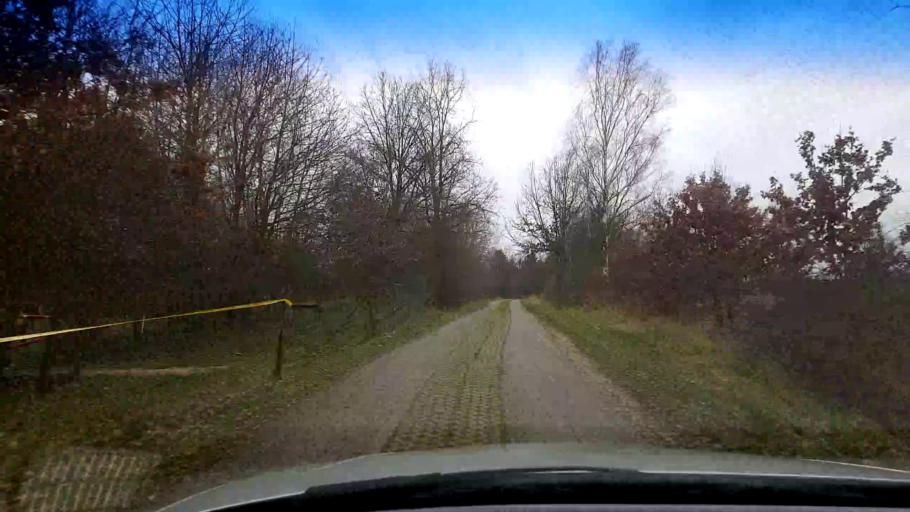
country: DE
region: Bavaria
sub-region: Upper Franconia
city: Baunach
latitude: 49.9791
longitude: 10.8349
